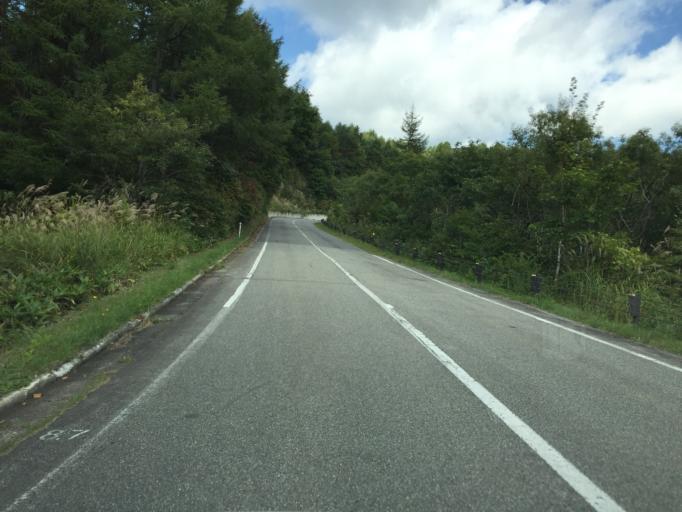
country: JP
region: Fukushima
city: Inawashiro
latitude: 37.6021
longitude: 140.0447
